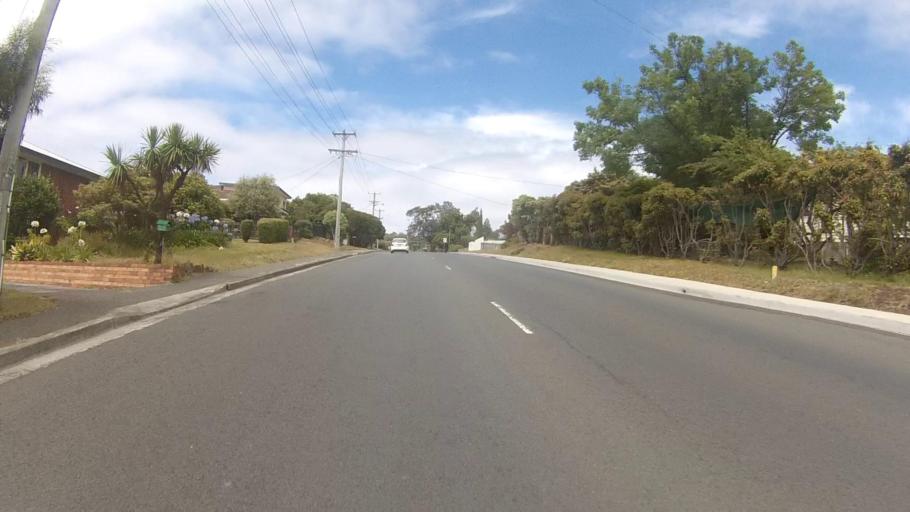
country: AU
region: Tasmania
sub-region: Kingborough
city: Blackmans Bay
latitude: -43.0044
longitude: 147.3191
